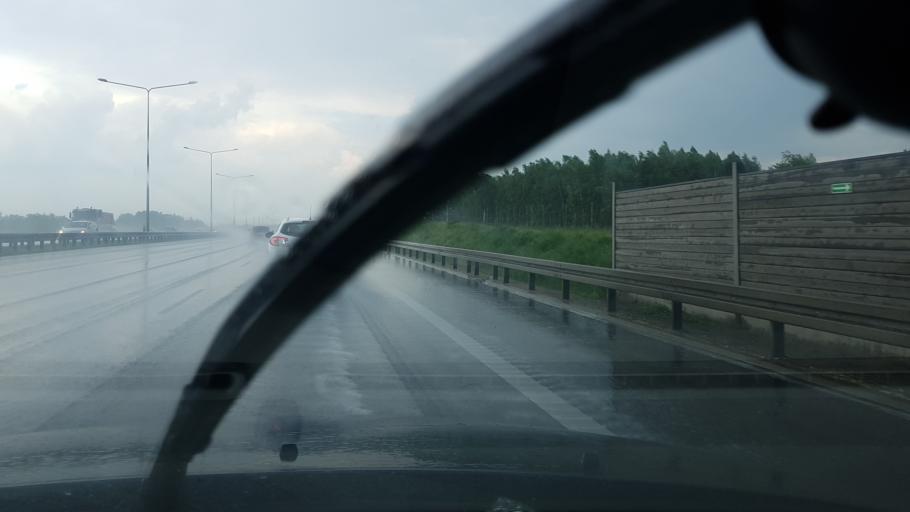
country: PL
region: Masovian Voivodeship
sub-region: Powiat pruszkowski
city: Nowe Grocholice
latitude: 52.1550
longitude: 20.8998
